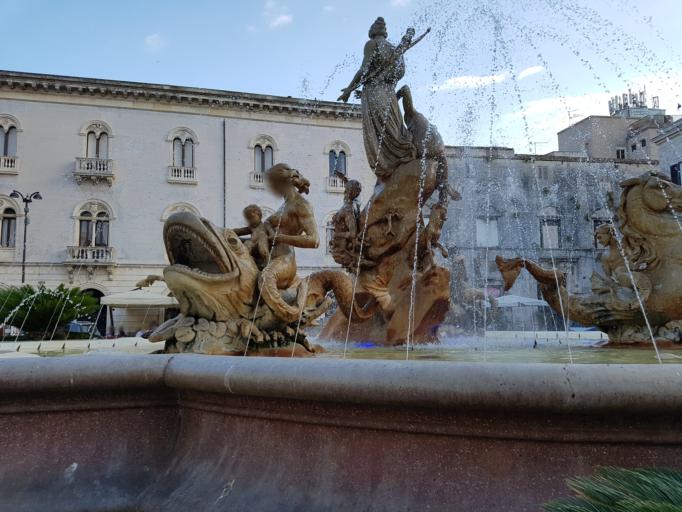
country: IT
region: Sicily
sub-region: Provincia di Siracusa
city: Siracusa
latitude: 37.0614
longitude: 15.2936
